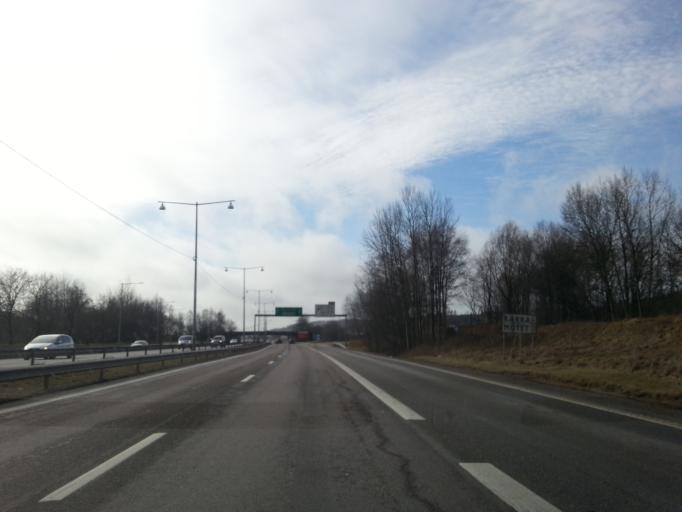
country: SE
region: Vaestra Goetaland
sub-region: Goteborg
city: Gardsten
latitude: 57.7907
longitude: 12.0016
